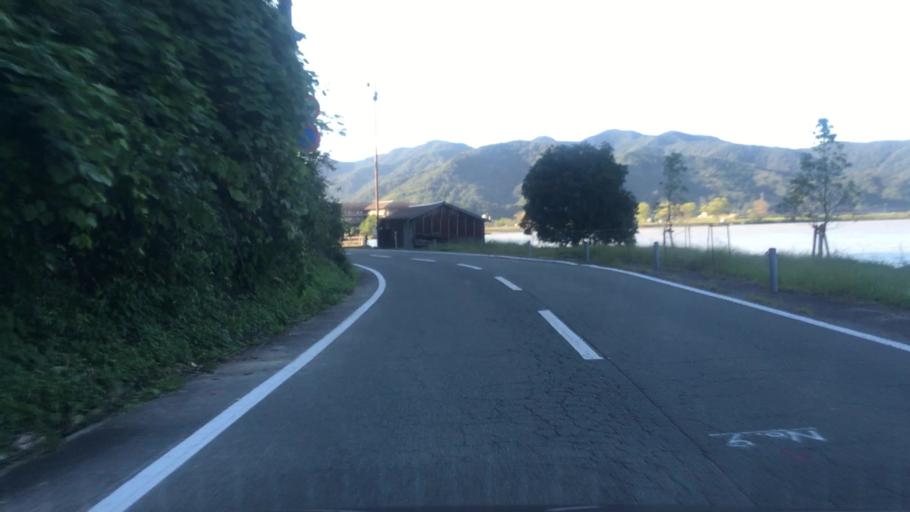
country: JP
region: Hyogo
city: Toyooka
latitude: 35.6174
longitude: 134.8230
